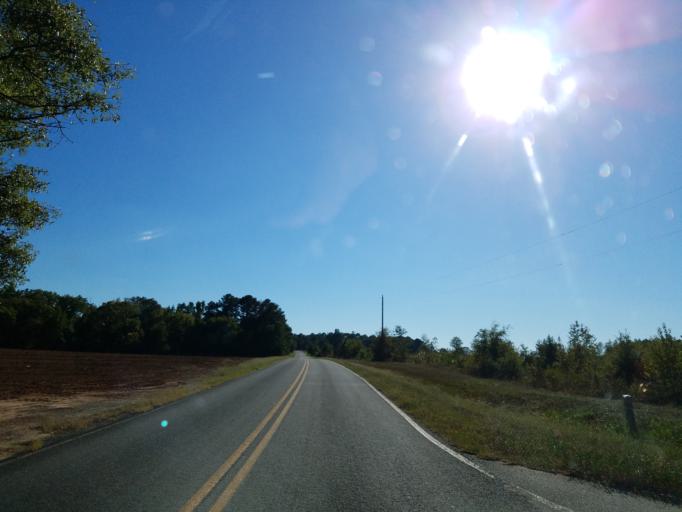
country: US
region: Georgia
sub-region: Dooly County
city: Unadilla
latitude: 32.2313
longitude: -83.8782
